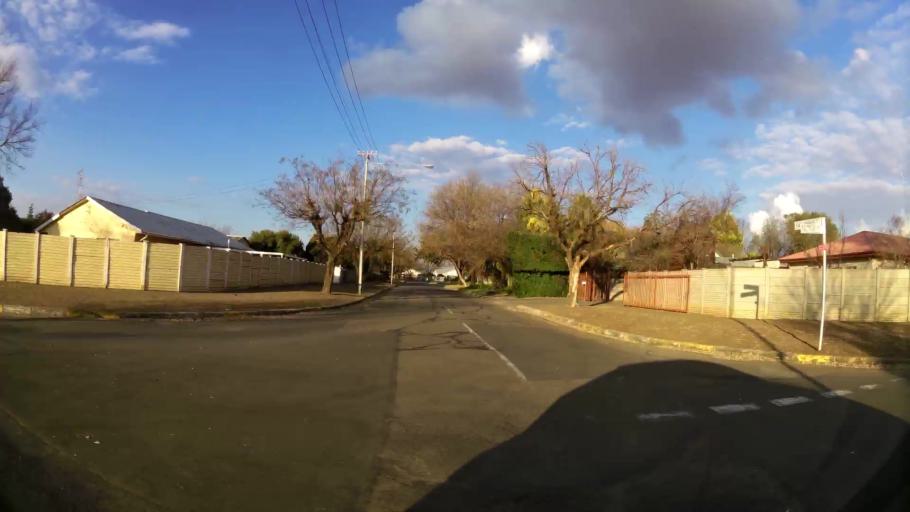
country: ZA
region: Orange Free State
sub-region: Mangaung Metropolitan Municipality
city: Bloemfontein
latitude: -29.1365
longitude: 26.1906
